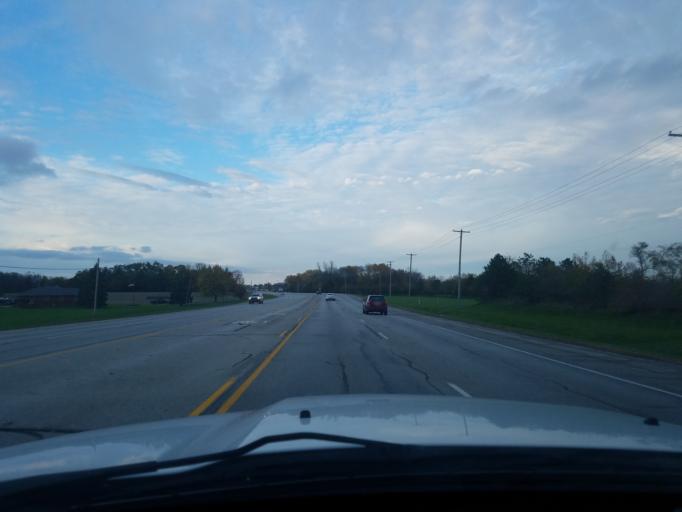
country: US
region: Indiana
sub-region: Shelby County
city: Shelbyville
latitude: 39.5381
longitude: -85.7758
